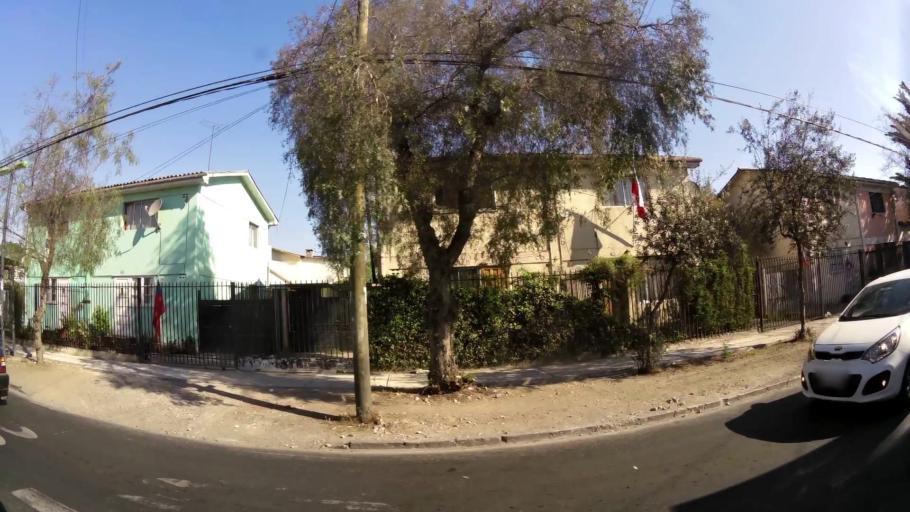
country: CL
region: Santiago Metropolitan
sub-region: Provincia de Santiago
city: Santiago
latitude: -33.4790
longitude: -70.6608
